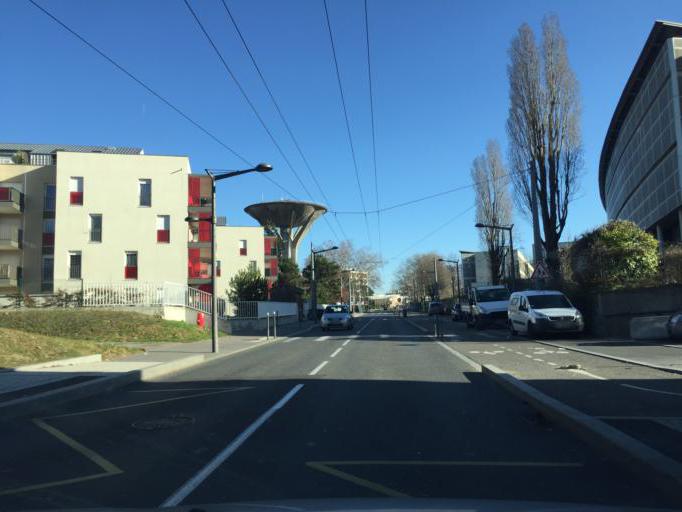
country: FR
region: Rhone-Alpes
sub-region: Departement du Rhone
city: Ecully
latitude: 45.7894
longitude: 4.7940
